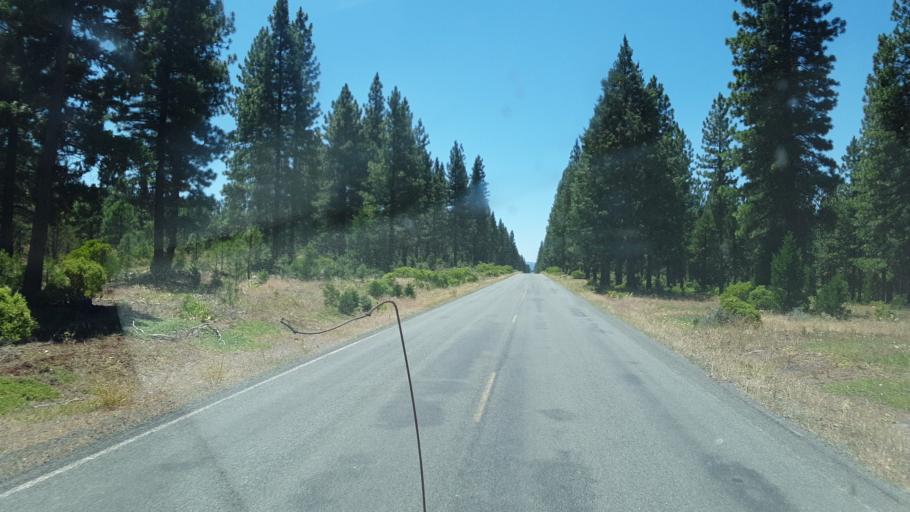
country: US
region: California
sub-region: Siskiyou County
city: Tulelake
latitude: 41.4250
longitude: -121.1703
